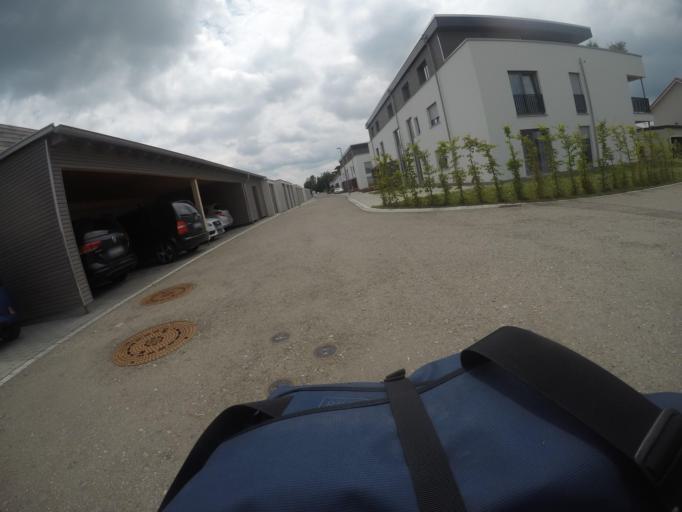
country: DE
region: Bavaria
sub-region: Swabia
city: Heimertingen
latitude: 48.0454
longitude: 10.1591
